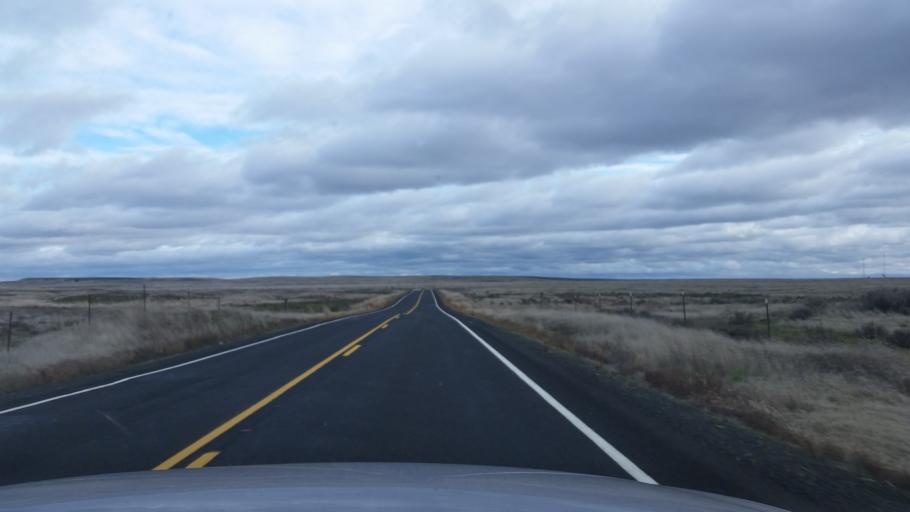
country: US
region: Washington
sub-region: Lincoln County
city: Davenport
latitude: 47.3339
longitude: -117.9904
